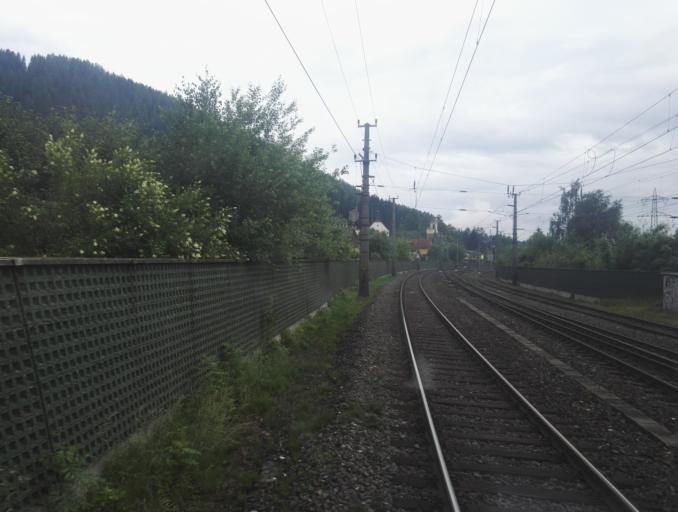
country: AT
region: Styria
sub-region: Politischer Bezirk Bruck-Muerzzuschlag
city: Kindberg
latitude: 47.4992
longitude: 15.4460
